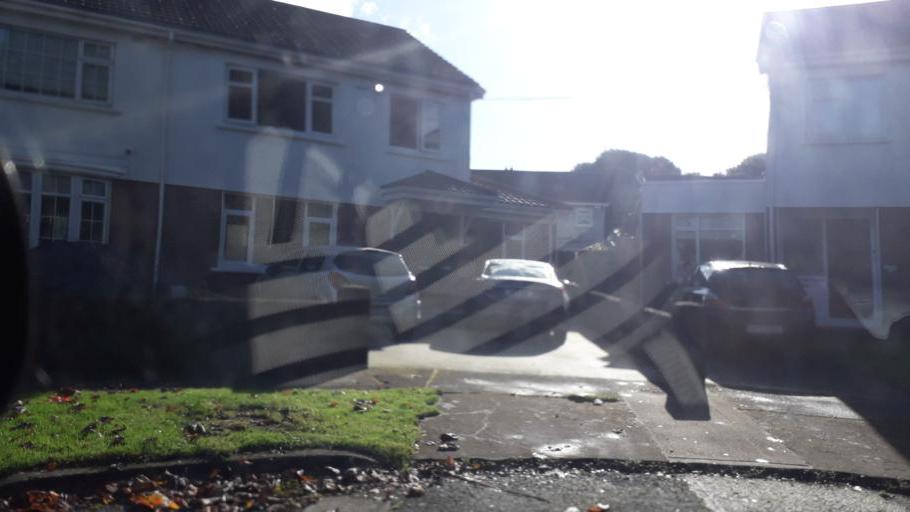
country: IE
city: Killester
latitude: 53.3764
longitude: -6.1936
